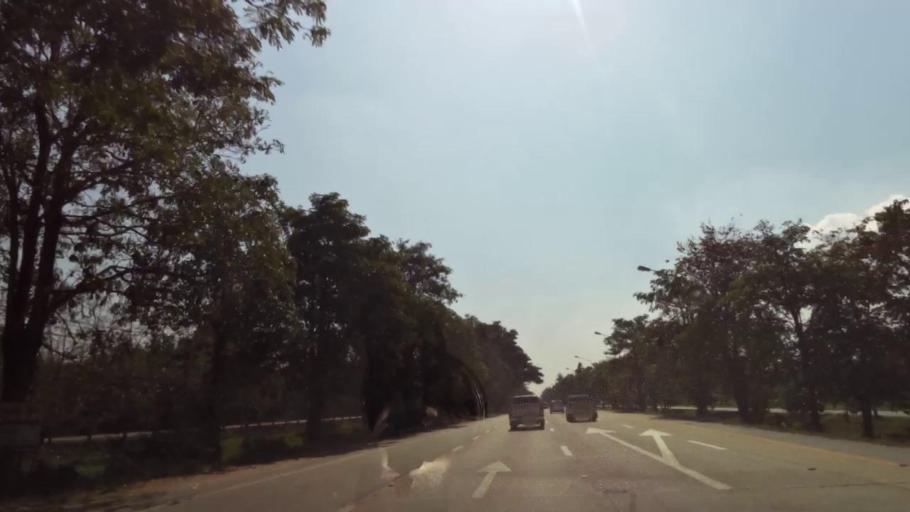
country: TH
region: Phichit
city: Wachira Barami
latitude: 16.5743
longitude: 100.1483
